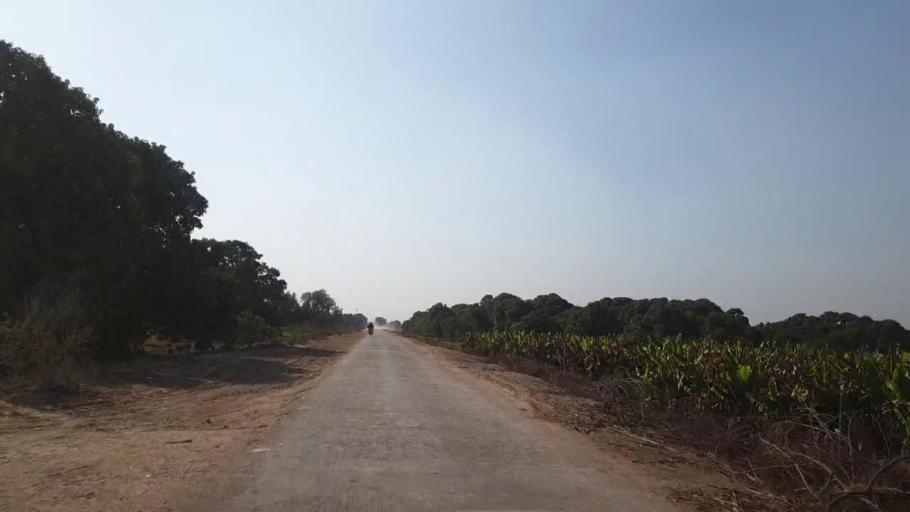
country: PK
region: Sindh
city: Tando Allahyar
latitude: 25.5689
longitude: 68.6964
